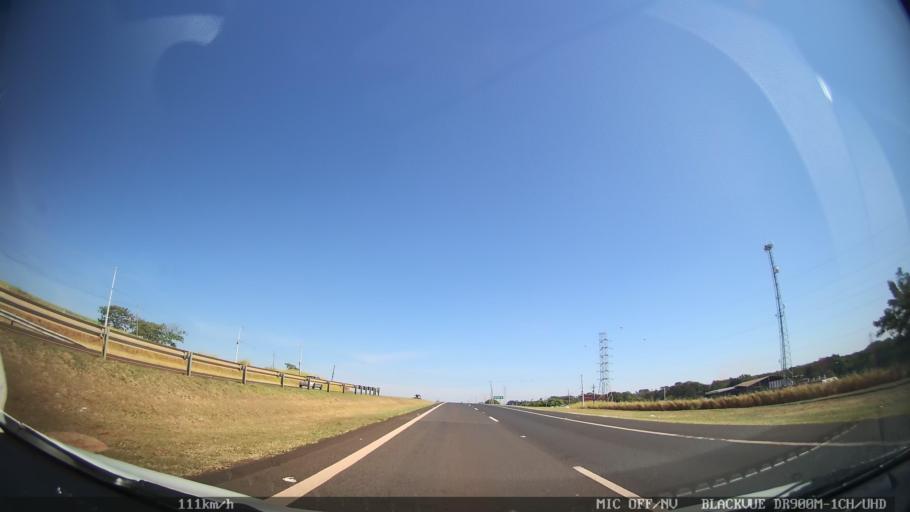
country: BR
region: Sao Paulo
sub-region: Ribeirao Preto
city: Ribeirao Preto
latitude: -21.1449
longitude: -47.8755
